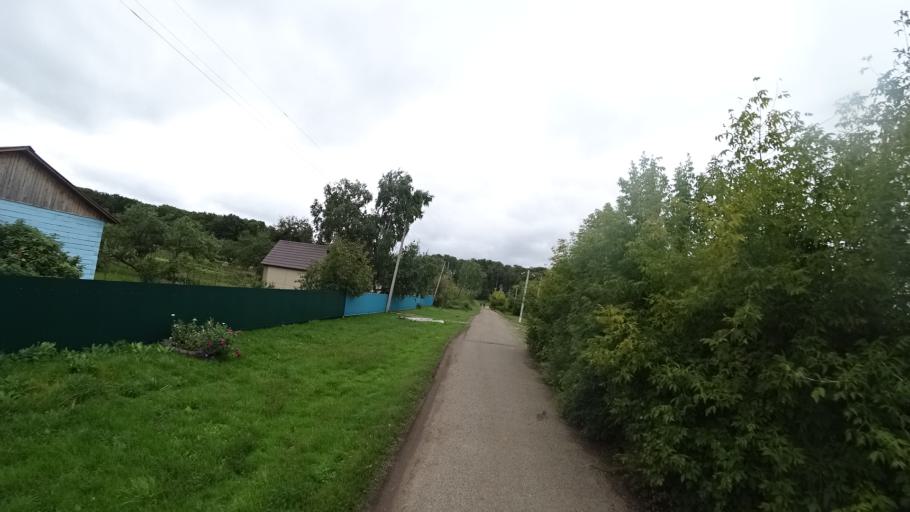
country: RU
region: Primorskiy
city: Chernigovka
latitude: 44.4542
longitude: 132.5931
